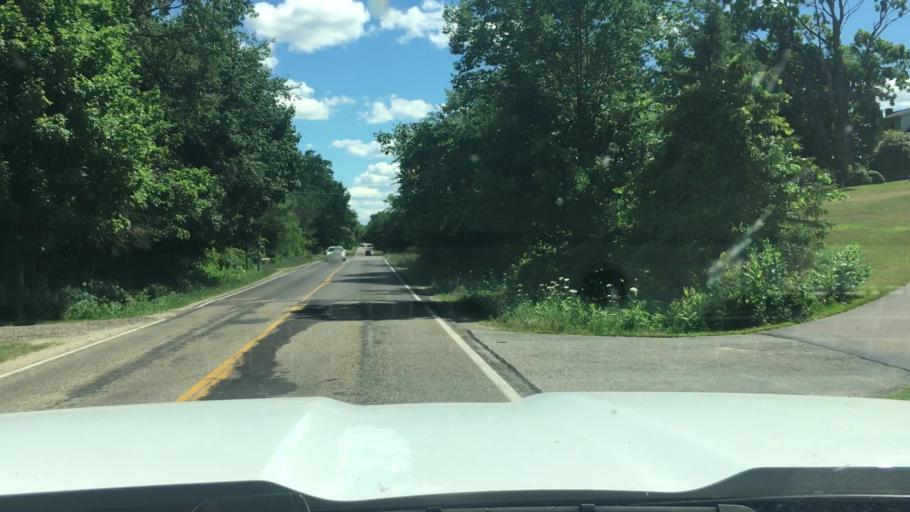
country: US
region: Michigan
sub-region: Kent County
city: Sparta
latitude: 43.1589
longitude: -85.6411
